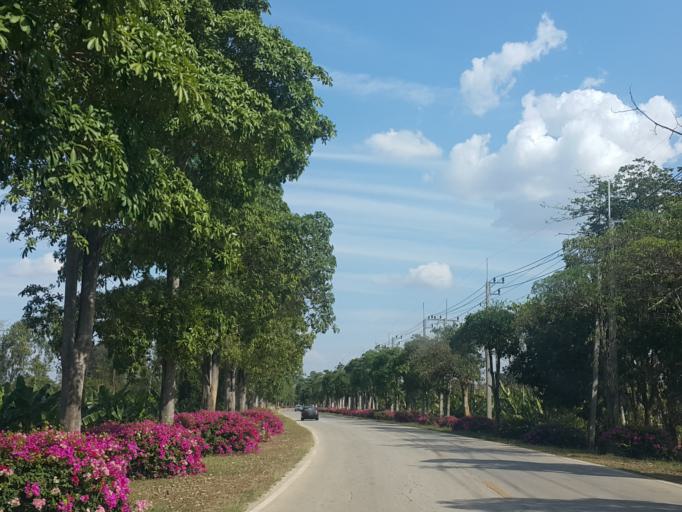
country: TH
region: Sukhothai
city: Si Samrong
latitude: 17.2283
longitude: 99.8398
